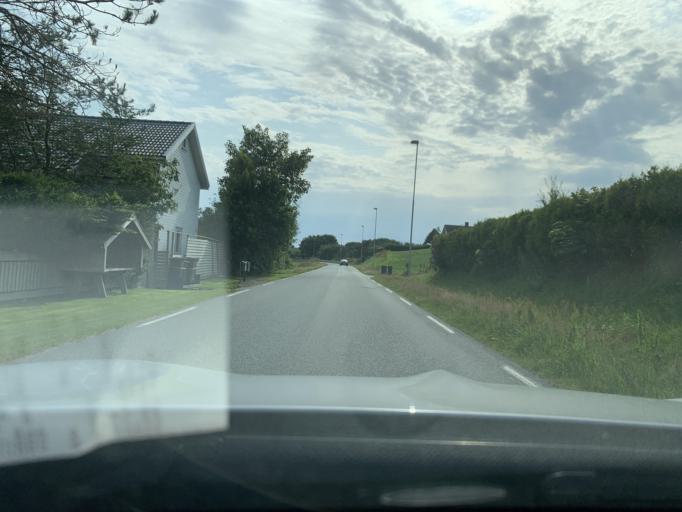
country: NO
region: Rogaland
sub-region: Time
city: Bryne
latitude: 58.7357
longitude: 5.6035
